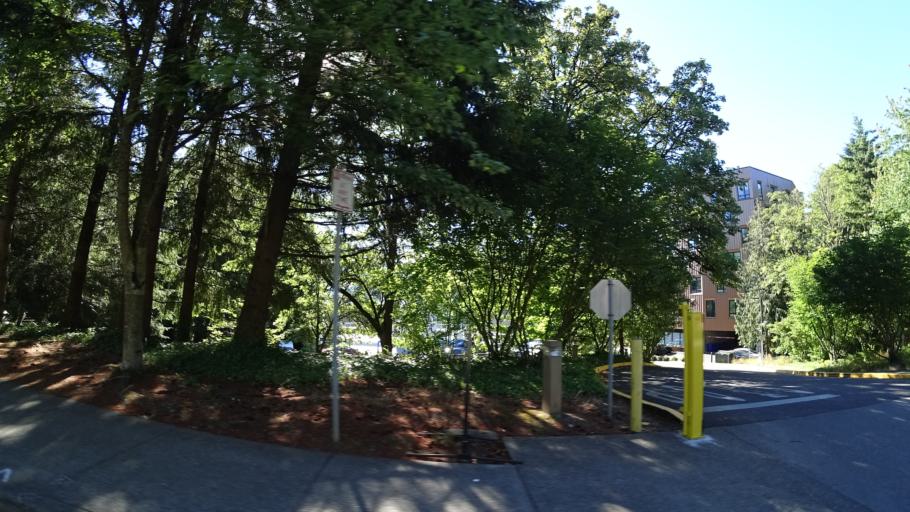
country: US
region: Oregon
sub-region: Multnomah County
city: Portland
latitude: 45.4983
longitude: -122.6896
